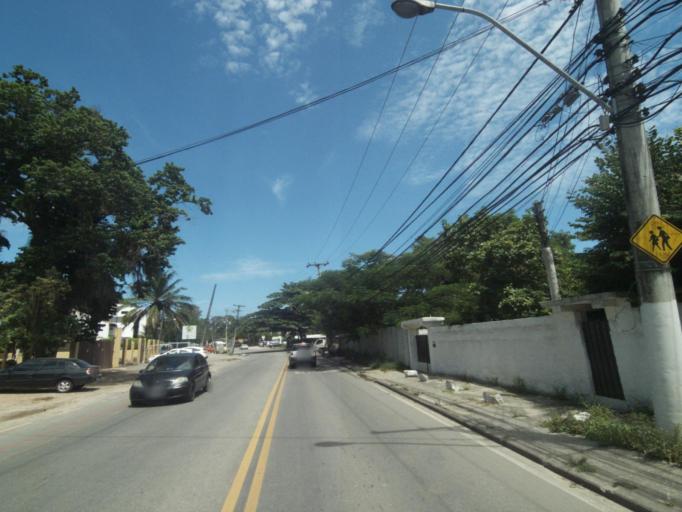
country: BR
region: Rio de Janeiro
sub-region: Niteroi
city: Niteroi
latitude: -22.9491
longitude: -43.0244
